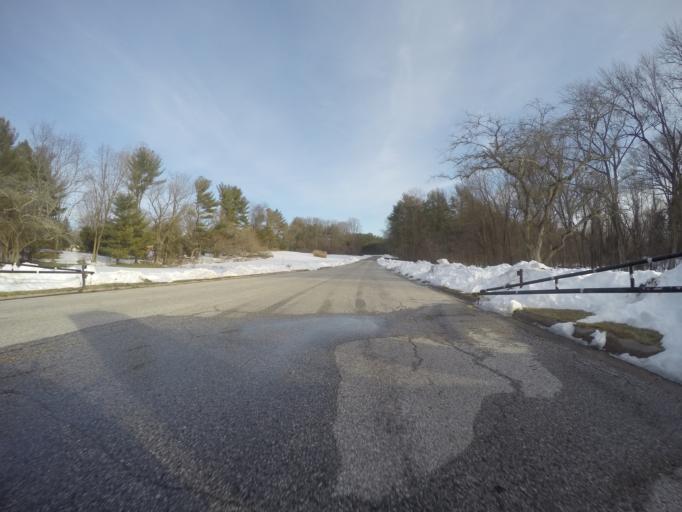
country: US
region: Maryland
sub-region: Baltimore County
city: Hampton
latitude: 39.4463
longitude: -76.5951
